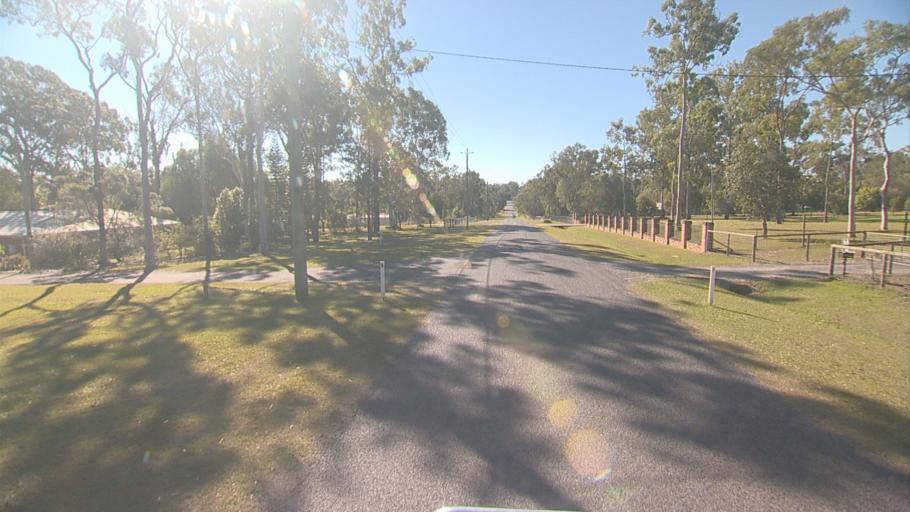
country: AU
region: Queensland
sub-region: Logan
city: Chambers Flat
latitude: -27.7389
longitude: 153.0705
